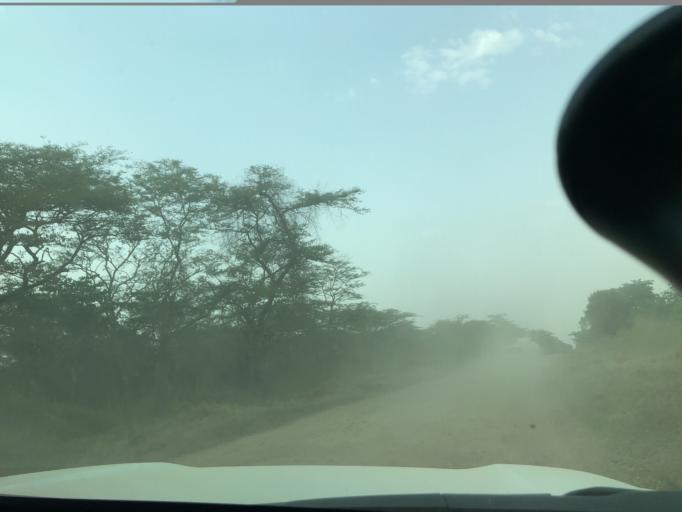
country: CD
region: Nord Kivu
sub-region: North Kivu
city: Butembo
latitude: 0.1511
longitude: 29.6404
